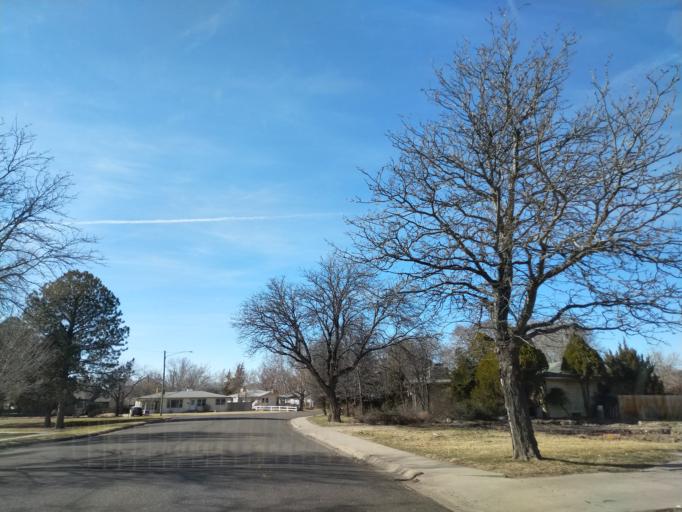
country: US
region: Colorado
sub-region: Mesa County
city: Grand Junction
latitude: 39.0824
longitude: -108.5665
